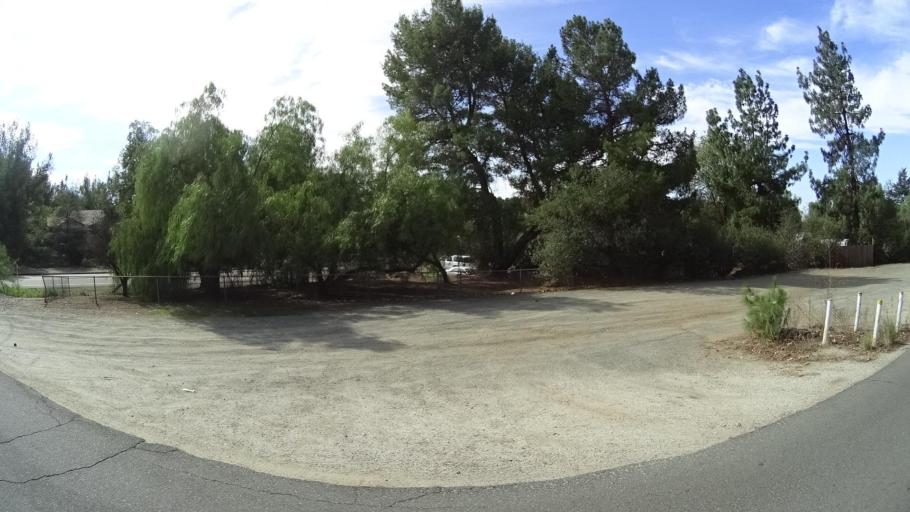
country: US
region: California
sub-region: San Diego County
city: Alpine
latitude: 32.8349
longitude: -116.7787
